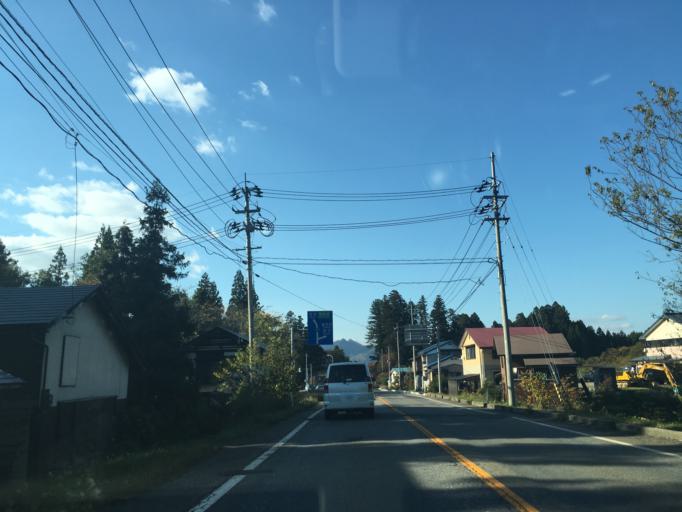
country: JP
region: Fukushima
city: Kitakata
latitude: 37.5774
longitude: 139.6604
